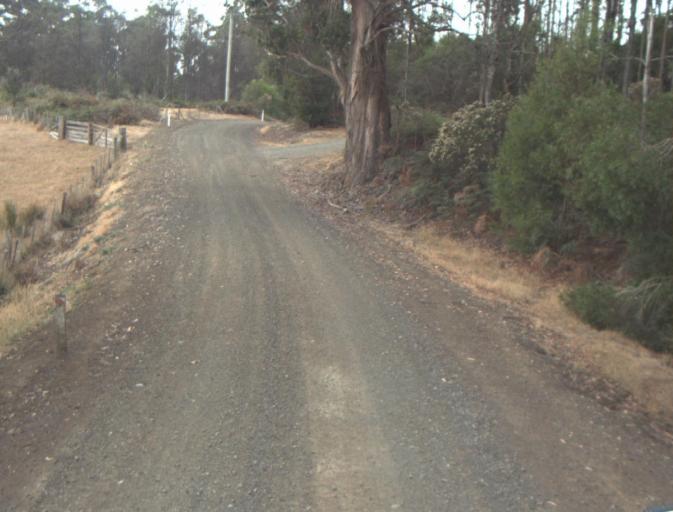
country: AU
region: Tasmania
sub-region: Launceston
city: Mayfield
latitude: -41.1987
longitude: 147.2298
